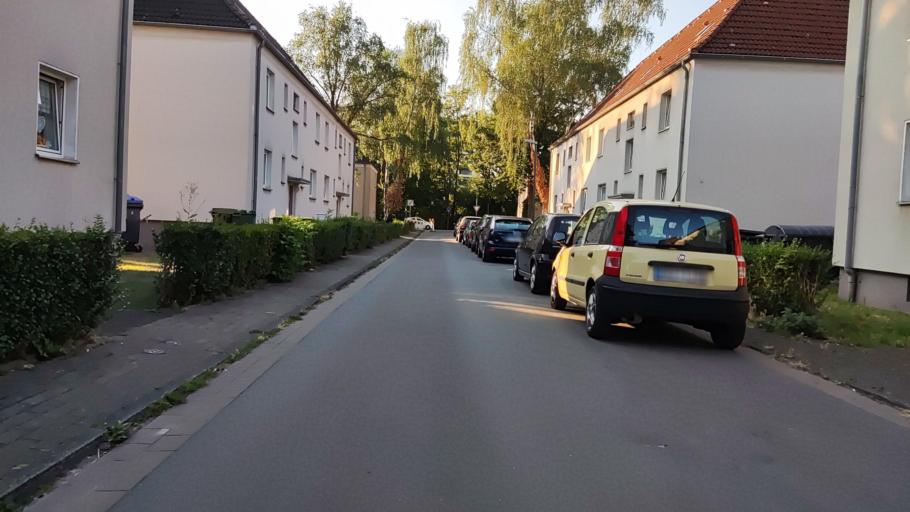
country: DE
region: North Rhine-Westphalia
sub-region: Regierungsbezirk Arnsberg
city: Herne
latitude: 51.5322
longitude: 7.2313
